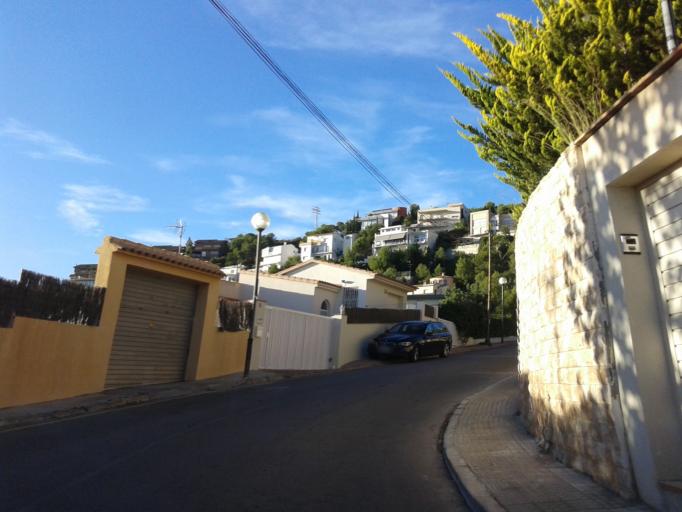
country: ES
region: Catalonia
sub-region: Provincia de Barcelona
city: Sitges
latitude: 41.2418
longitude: 1.8285
